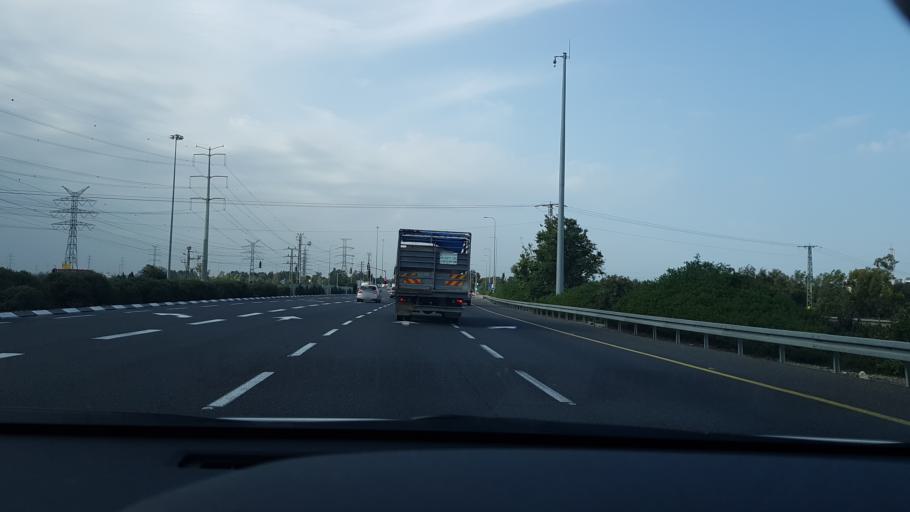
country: IL
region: Southern District
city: Ashdod
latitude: 31.7854
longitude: 34.6746
